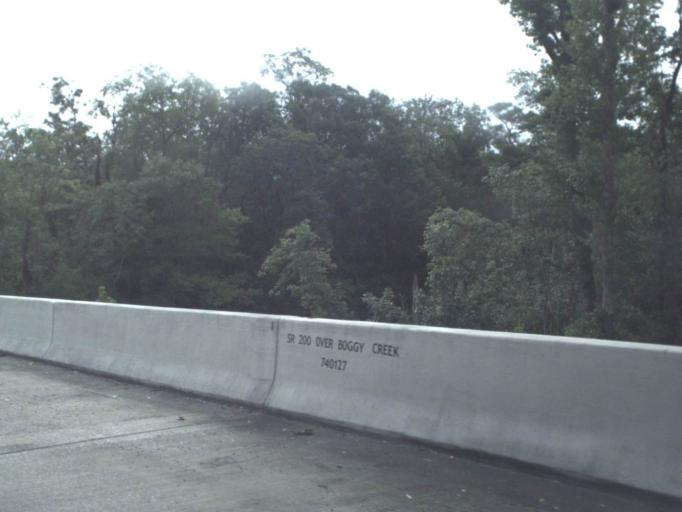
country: US
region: Florida
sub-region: Nassau County
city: Callahan
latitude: 30.6081
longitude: -81.7422
